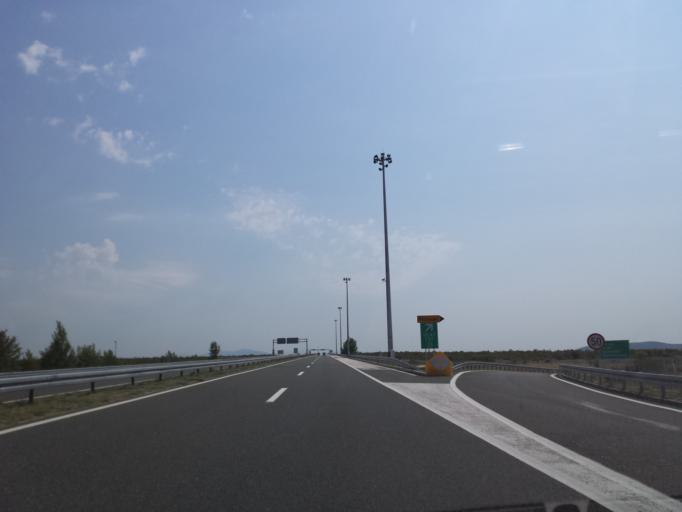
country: HR
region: Sibensko-Kniniska
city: Zaton
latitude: 43.8898
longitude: 15.7886
